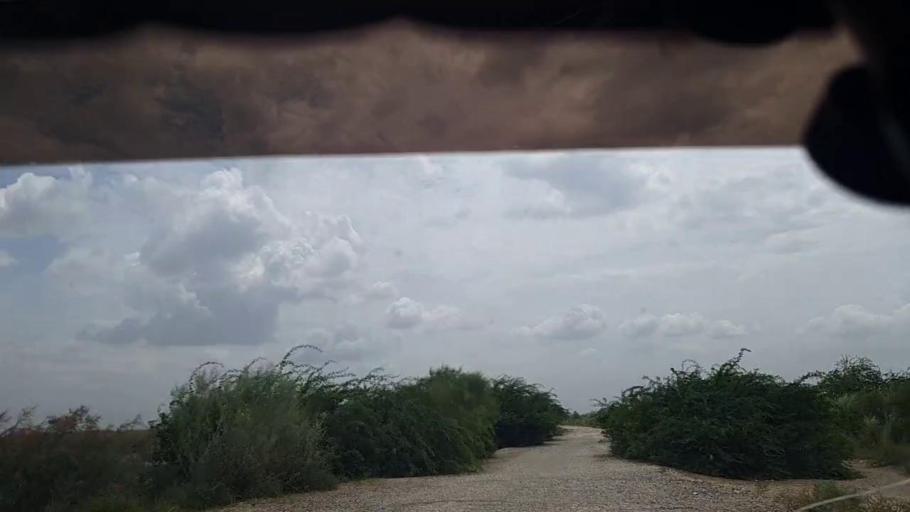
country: PK
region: Sindh
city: Rustam jo Goth
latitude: 28.0532
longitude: 68.9395
